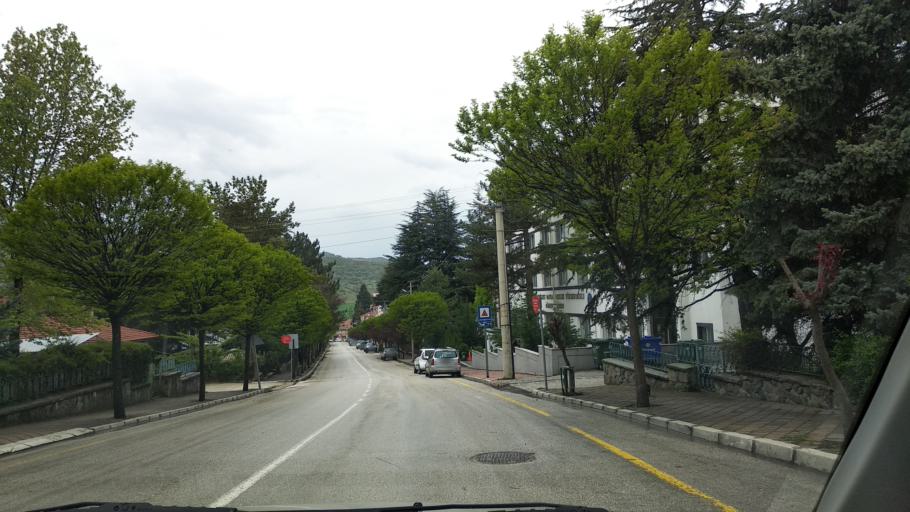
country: TR
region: Bolu
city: Seben
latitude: 40.4114
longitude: 31.5733
